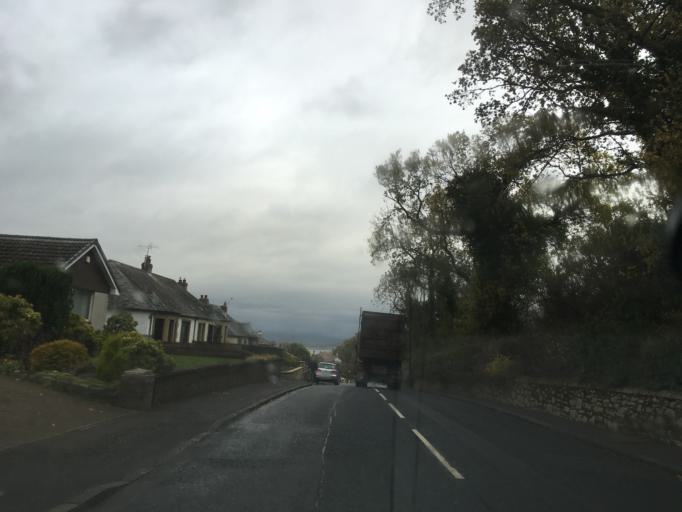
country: GB
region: Scotland
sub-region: Falkirk
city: Bo'ness
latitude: 56.0085
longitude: -3.5755
